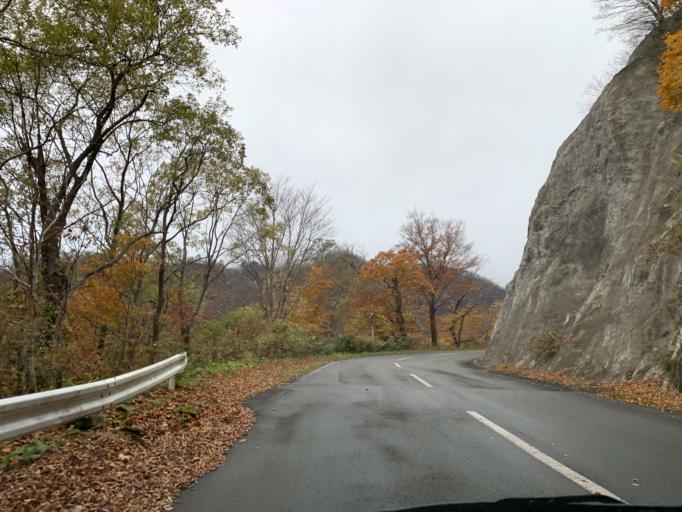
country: JP
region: Iwate
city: Mizusawa
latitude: 39.1215
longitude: 140.8318
